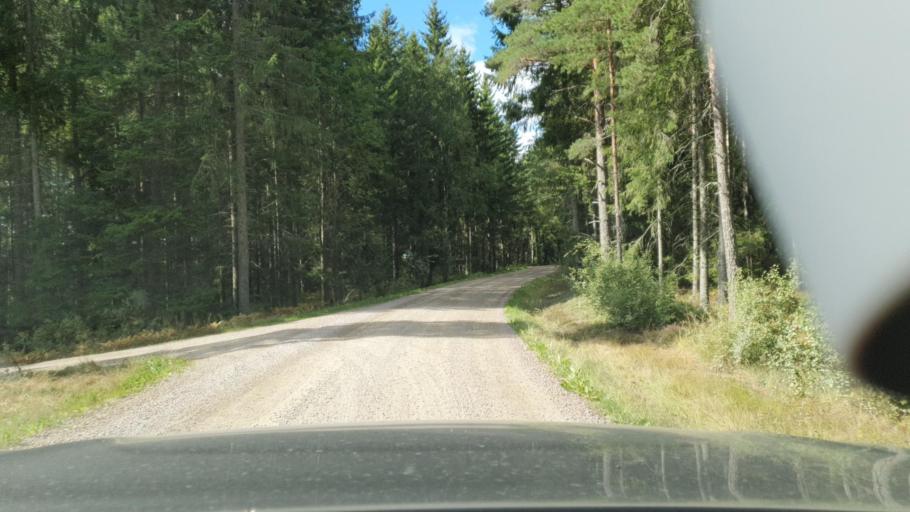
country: SE
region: Vaermland
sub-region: Karlstads Kommun
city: Molkom
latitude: 59.5598
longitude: 13.7320
